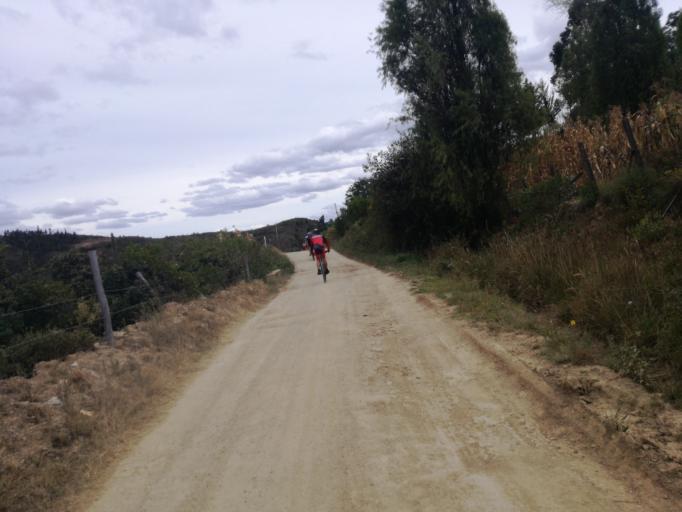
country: CO
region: Boyaca
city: Socha Viejo
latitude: 6.0092
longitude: -72.6850
